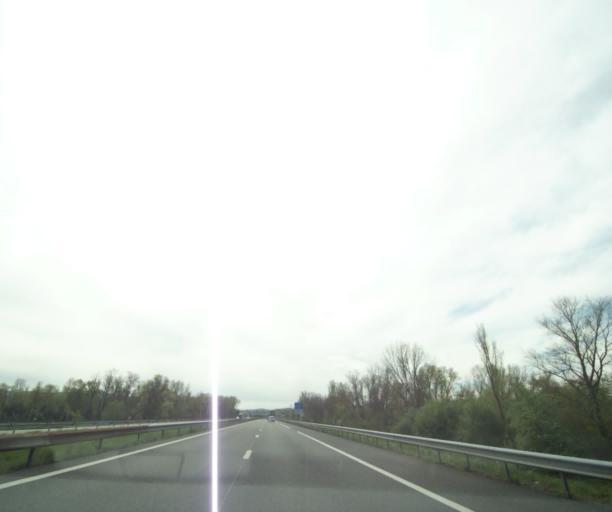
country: FR
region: Rhone-Alpes
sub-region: Departement du Rhone
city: Anse
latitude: 45.9106
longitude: 4.7274
